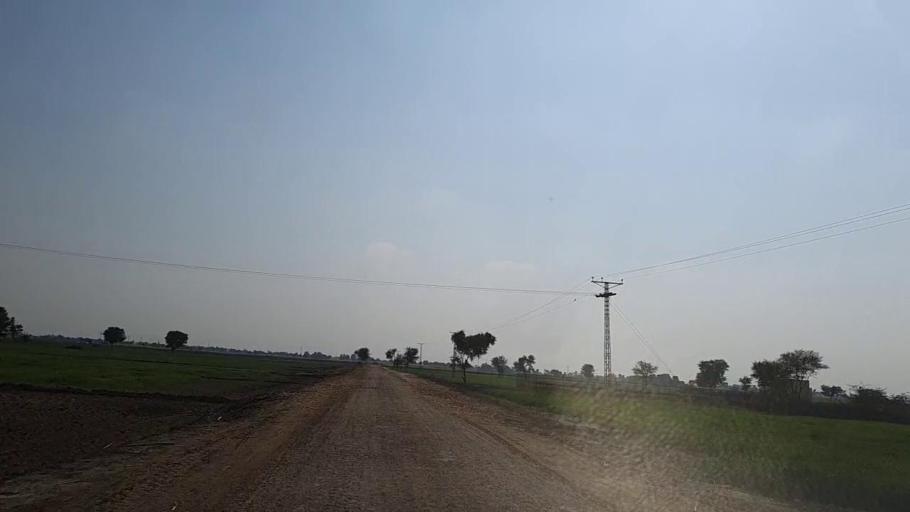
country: PK
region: Sindh
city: Daur
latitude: 26.4475
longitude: 68.2347
